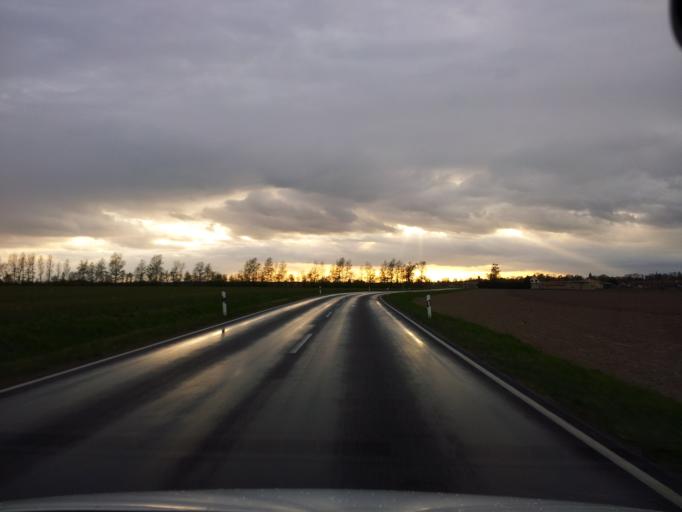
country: DE
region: Brandenburg
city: Dahme
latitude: 51.8612
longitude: 13.4523
